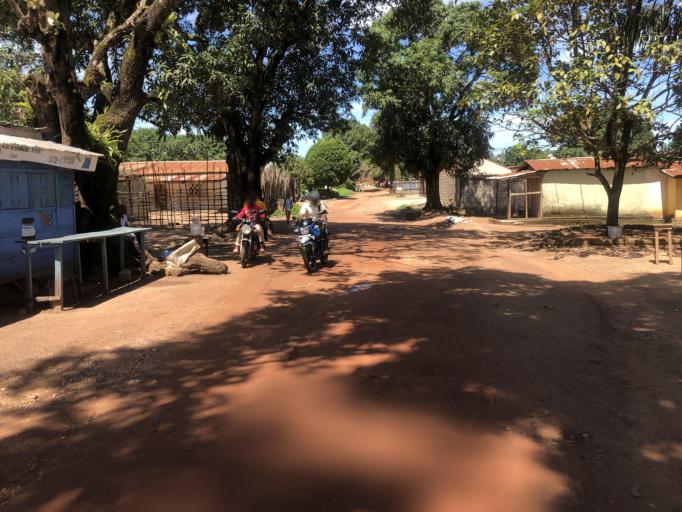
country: SL
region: Eastern Province
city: Koidu
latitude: 8.6415
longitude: -10.9643
